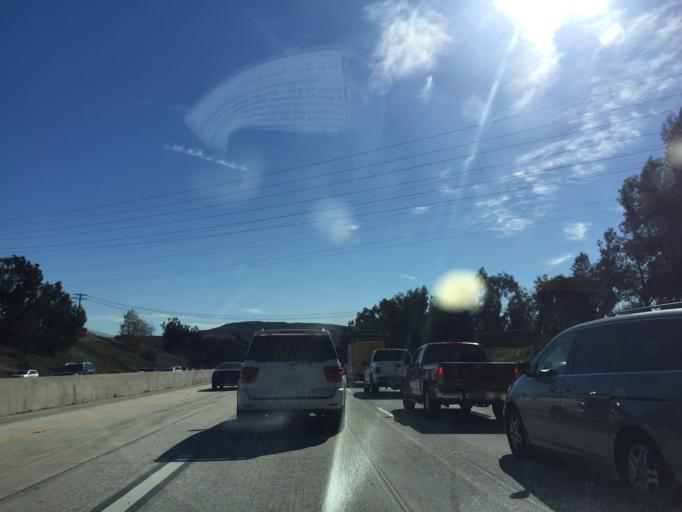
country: US
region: California
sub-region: Orange County
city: San Juan Capistrano
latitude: 33.5131
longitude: -117.6627
